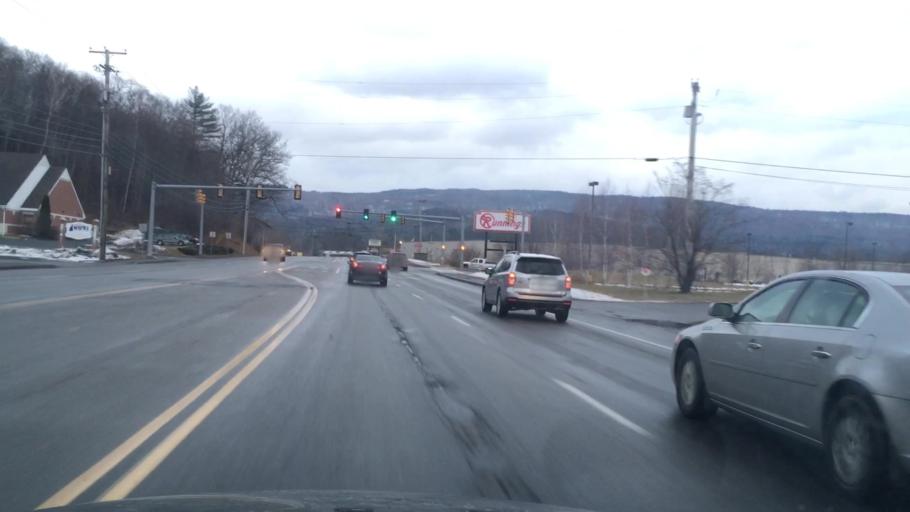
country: US
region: New Hampshire
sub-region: Sullivan County
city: Claremont
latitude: 43.3627
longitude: -72.3152
